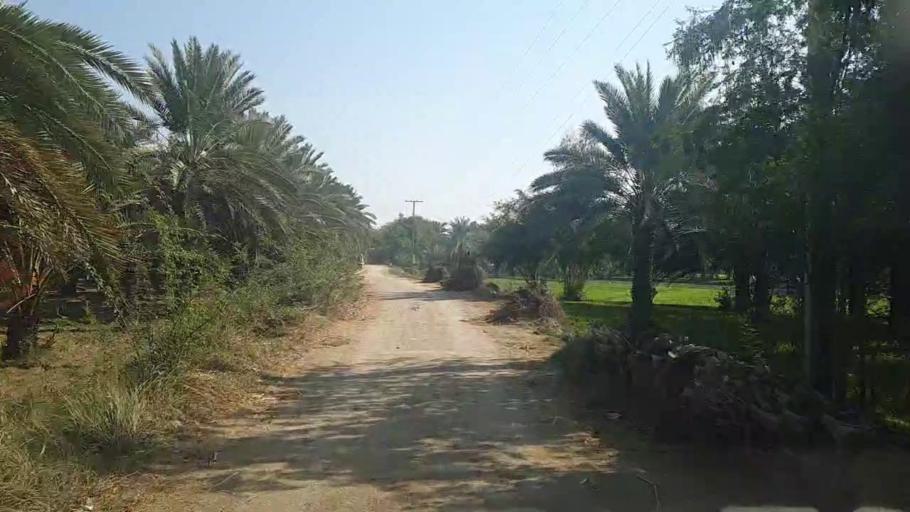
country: PK
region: Sindh
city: Kot Diji
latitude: 27.4331
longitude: 68.7199
